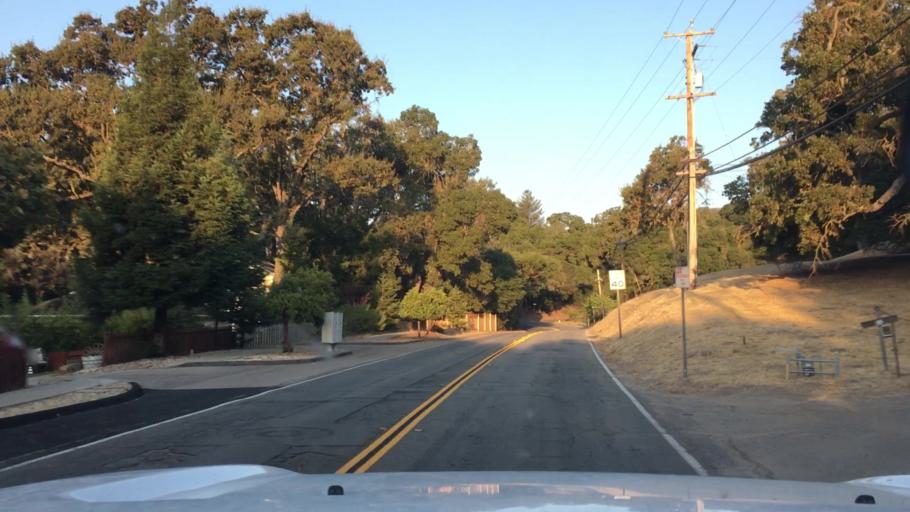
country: US
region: California
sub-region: San Luis Obispo County
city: Atascadero
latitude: 35.4840
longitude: -120.6765
